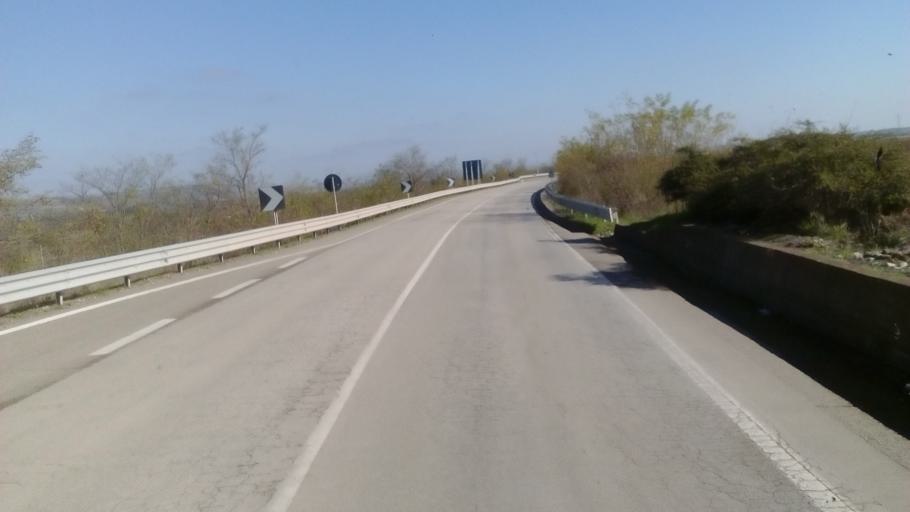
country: IT
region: Basilicate
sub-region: Provincia di Potenza
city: Zona 179
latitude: 41.0825
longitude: 15.6197
